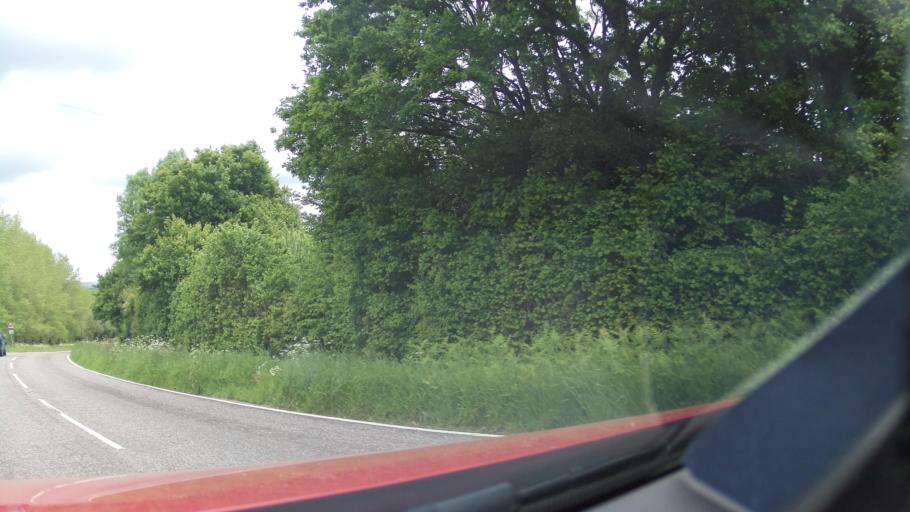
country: GB
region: England
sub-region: Dorset
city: Sherborne
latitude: 50.8484
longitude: -2.4876
